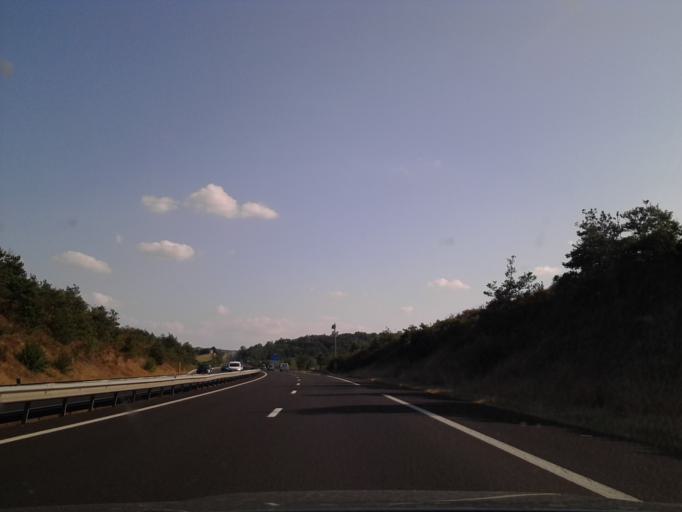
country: FR
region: Auvergne
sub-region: Departement de la Haute-Loire
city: Lempdes-sur-Allagnon
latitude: 45.3559
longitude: 3.2785
